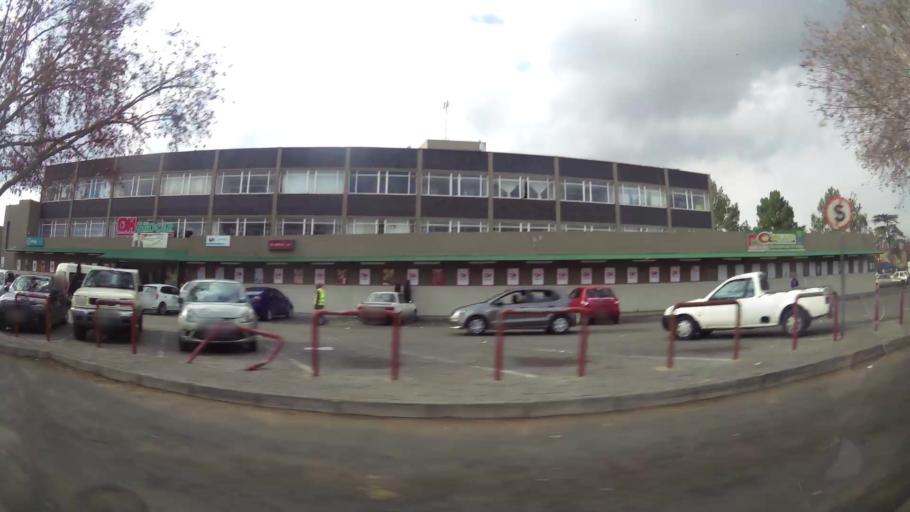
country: ZA
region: Orange Free State
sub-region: Fezile Dabi District Municipality
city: Sasolburg
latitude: -26.8198
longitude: 27.8338
